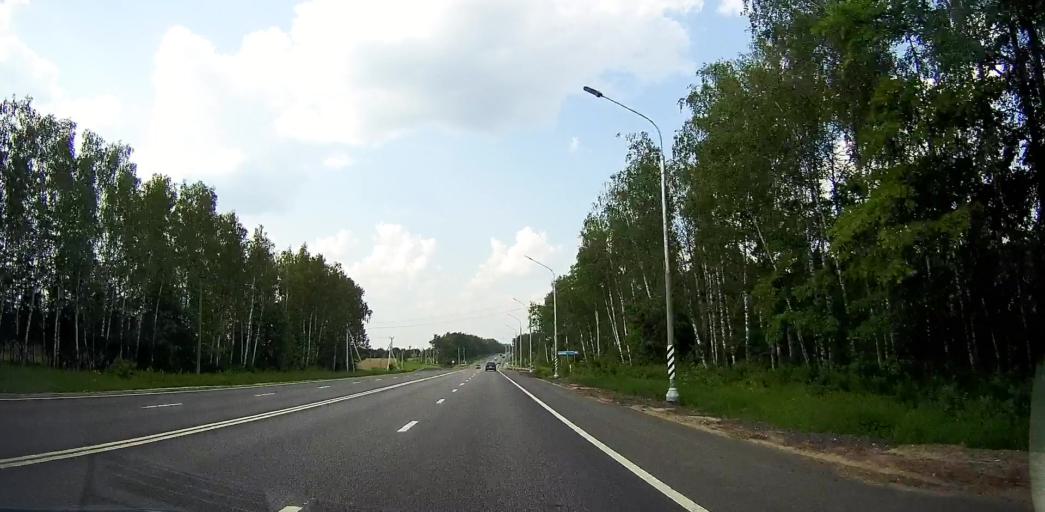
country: RU
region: Moskovskaya
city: Mikhnevo
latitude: 55.0929
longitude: 37.9531
